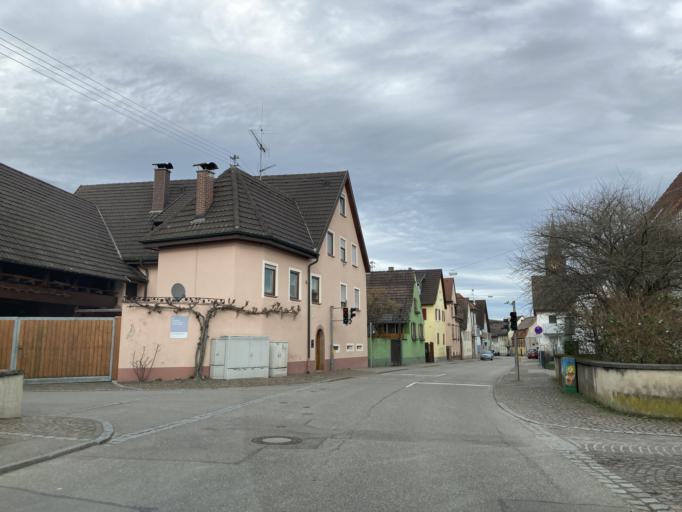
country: DE
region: Baden-Wuerttemberg
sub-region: Freiburg Region
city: Botzingen
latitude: 48.0739
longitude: 7.7222
